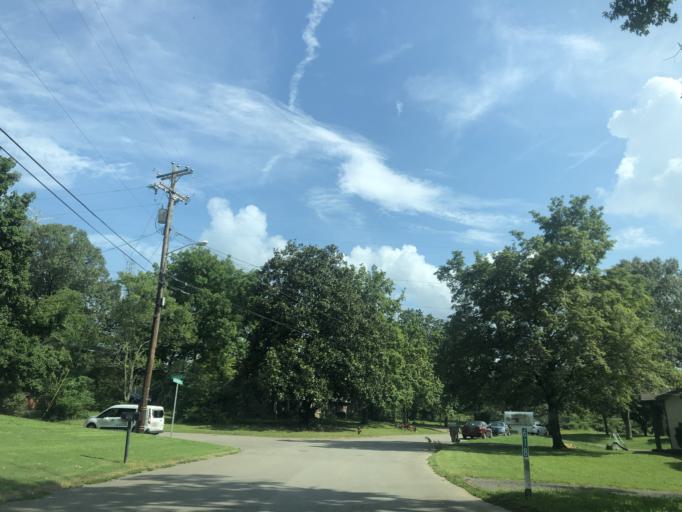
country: US
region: Tennessee
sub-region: Davidson County
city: Lakewood
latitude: 36.1611
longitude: -86.6283
